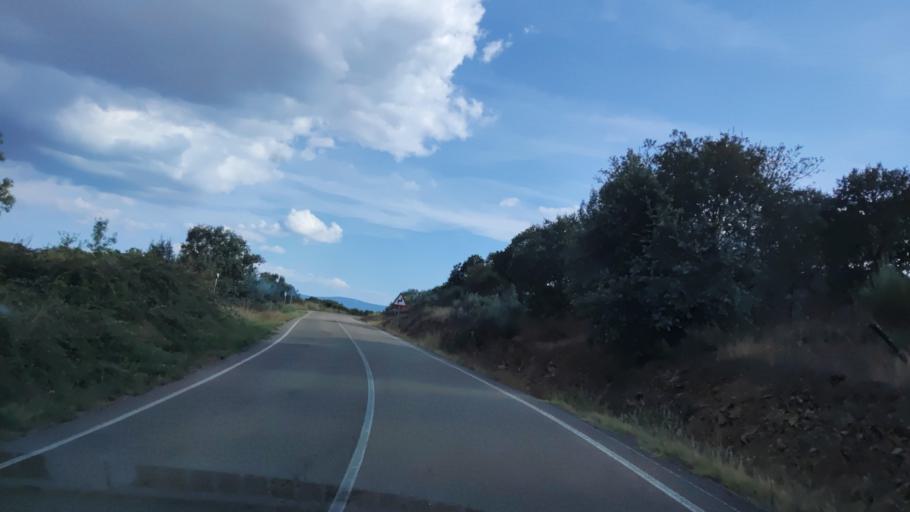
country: ES
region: Castille and Leon
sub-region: Provincia de Salamanca
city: Martiago
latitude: 40.4730
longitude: -6.4905
